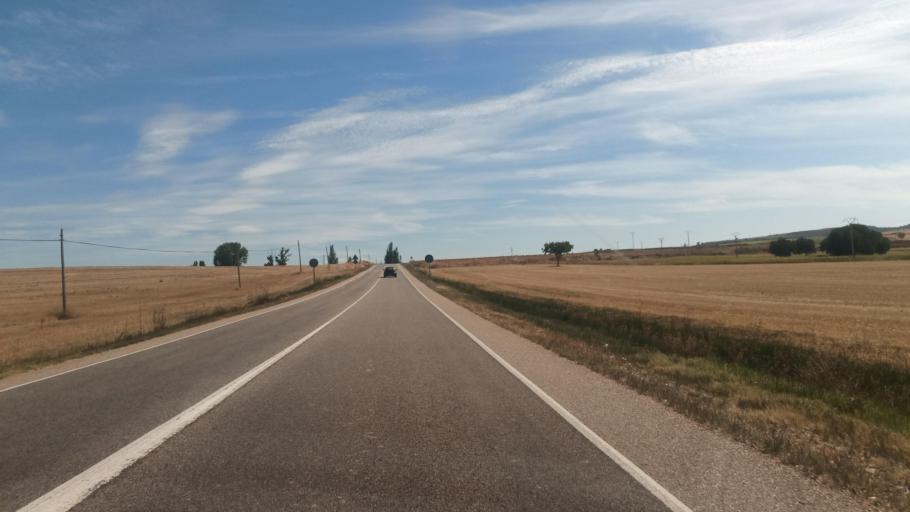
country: ES
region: Castille and Leon
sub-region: Provincia de Burgos
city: Aguilar de Bureba
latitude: 42.5870
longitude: -3.3397
